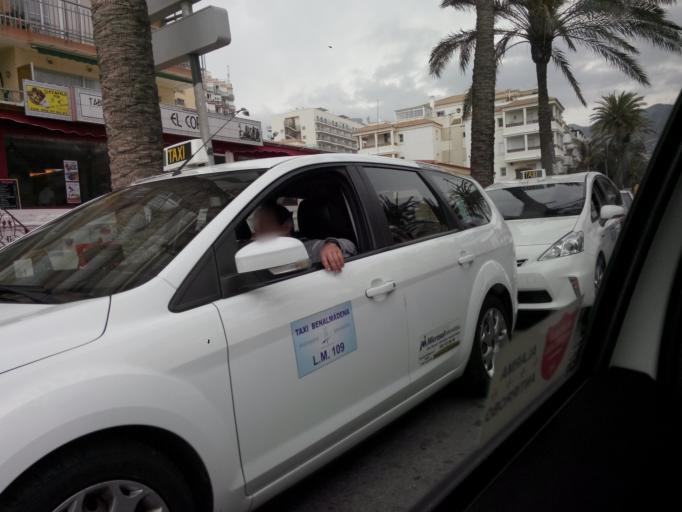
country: ES
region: Andalusia
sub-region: Provincia de Malaga
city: Benalmadena
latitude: 36.5882
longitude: -4.5315
